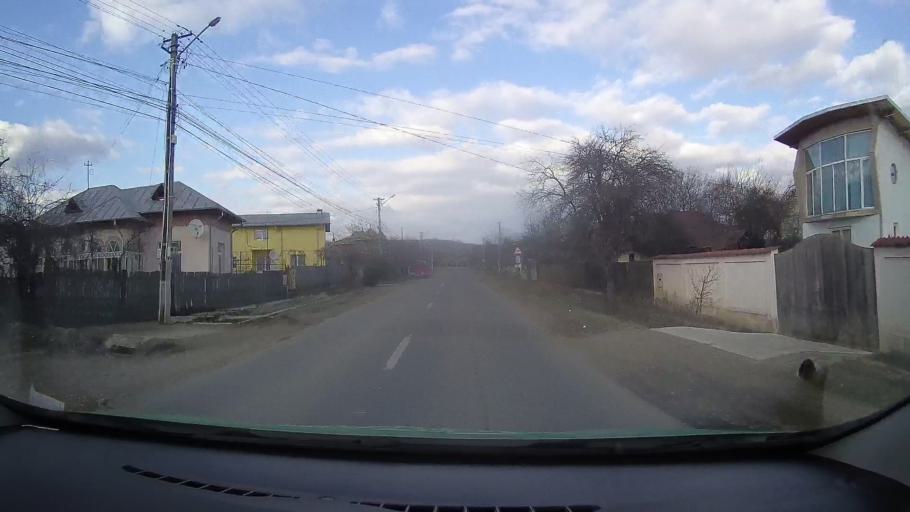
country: RO
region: Dambovita
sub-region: Comuna Gura Ocnitei
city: Gura Ocnitei
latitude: 44.9325
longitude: 25.5612
